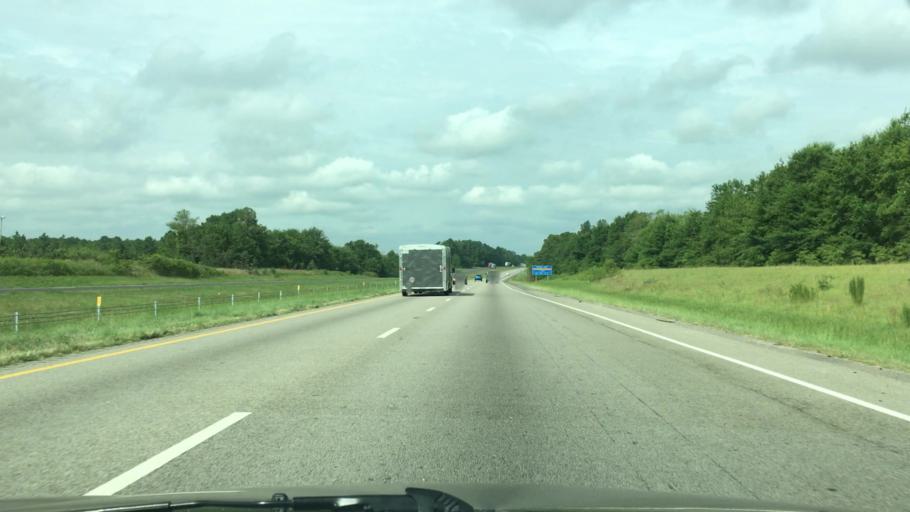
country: US
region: South Carolina
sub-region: Aiken County
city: Aiken
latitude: 33.6630
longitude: -81.6815
